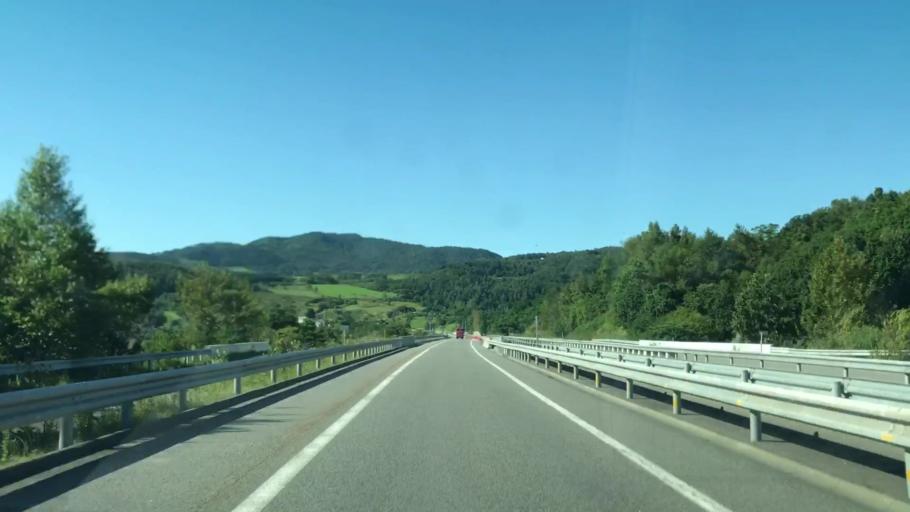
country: JP
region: Hokkaido
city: Date
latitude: 42.5431
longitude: 140.7940
